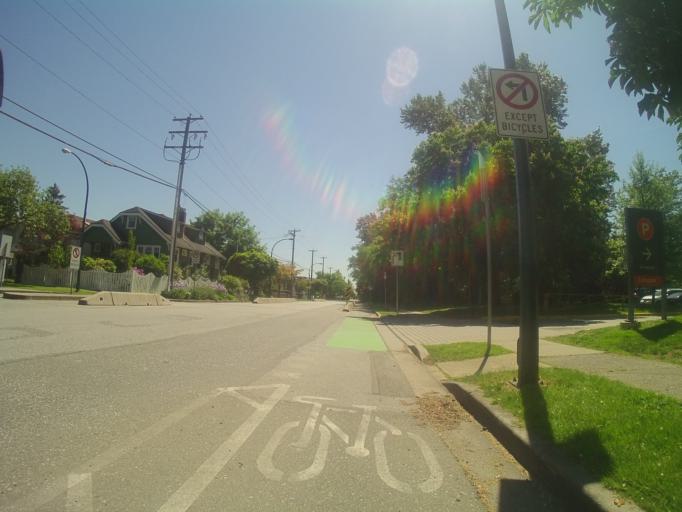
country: CA
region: British Columbia
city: Vancouver
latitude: 49.2241
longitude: -123.1061
